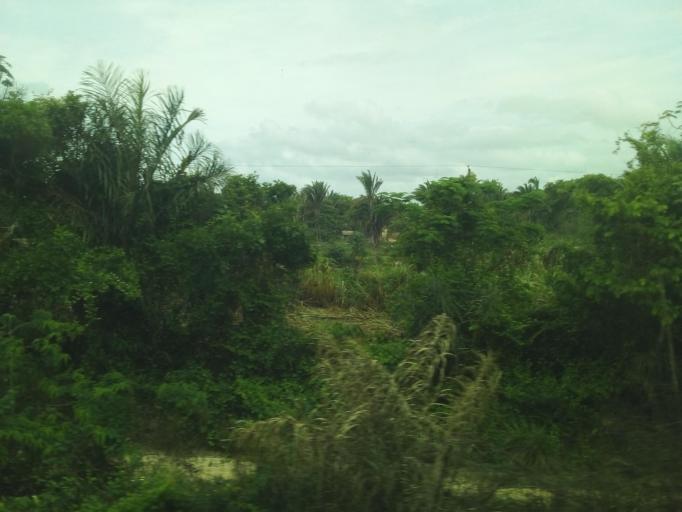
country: BR
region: Maranhao
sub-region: Itapecuru Mirim
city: Itapecuru Mirim
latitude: -3.3214
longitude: -44.4830
